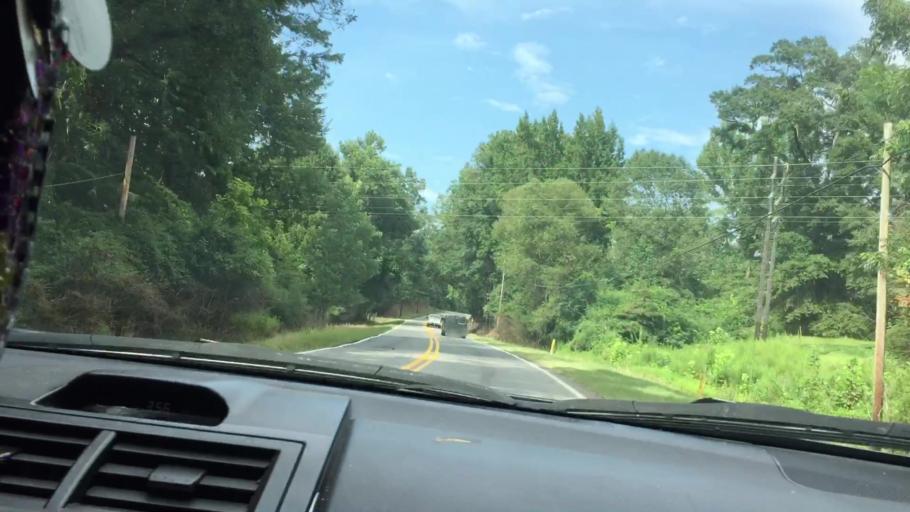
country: US
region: Alabama
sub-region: Hale County
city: Greensboro
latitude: 32.6944
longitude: -87.6048
